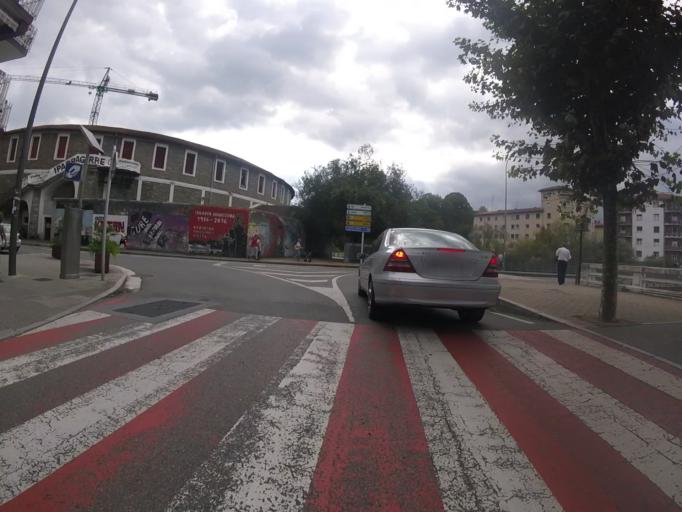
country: ES
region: Basque Country
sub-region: Provincia de Guipuzcoa
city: Tolosa
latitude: 43.1332
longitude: -2.0773
